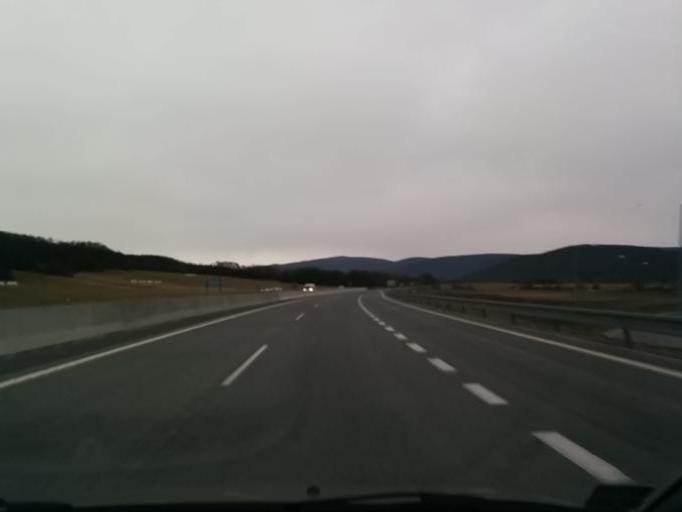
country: SK
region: Nitriansky
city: Tlmace
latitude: 48.3714
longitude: 18.5342
